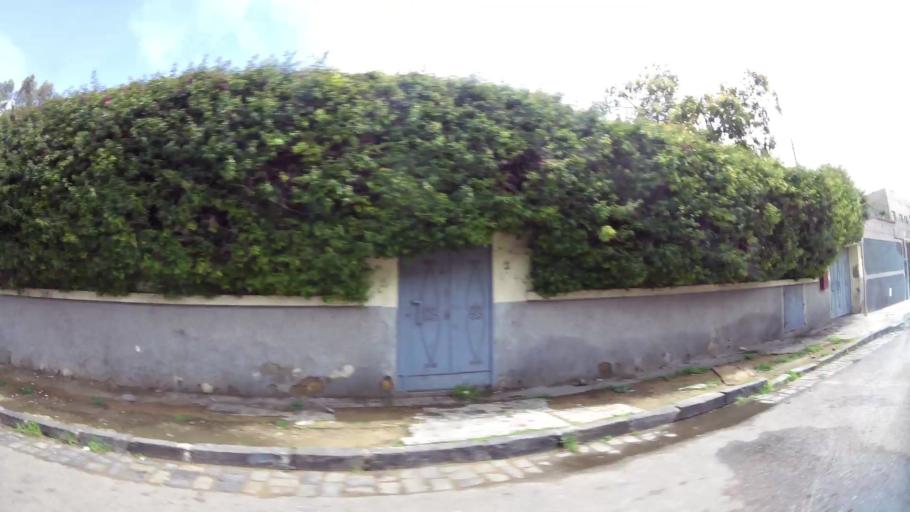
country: MA
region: Grand Casablanca
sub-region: Casablanca
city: Casablanca
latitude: 33.5677
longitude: -7.6296
